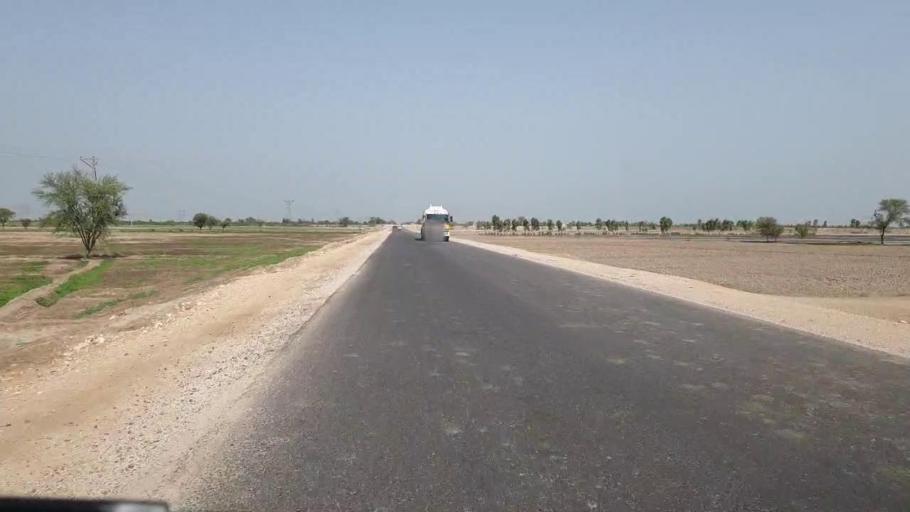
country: PK
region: Sindh
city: Sakrand
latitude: 26.2622
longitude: 68.1813
